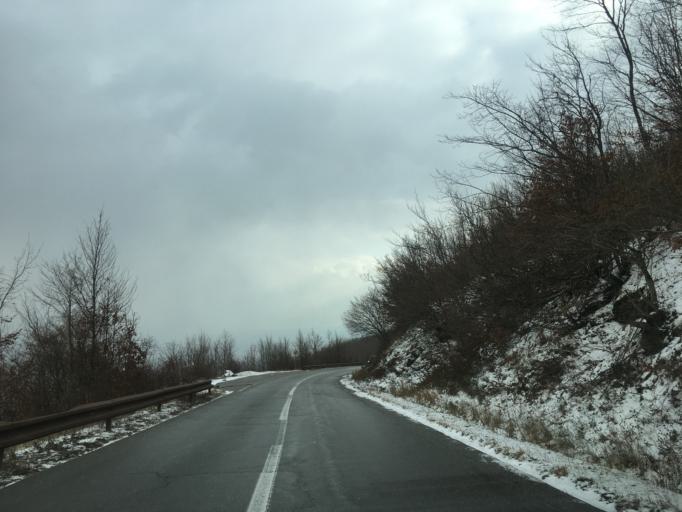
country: XK
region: Pec
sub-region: Komuna e Pejes
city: Dubova (Driloni)
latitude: 42.7533
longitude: 20.3011
